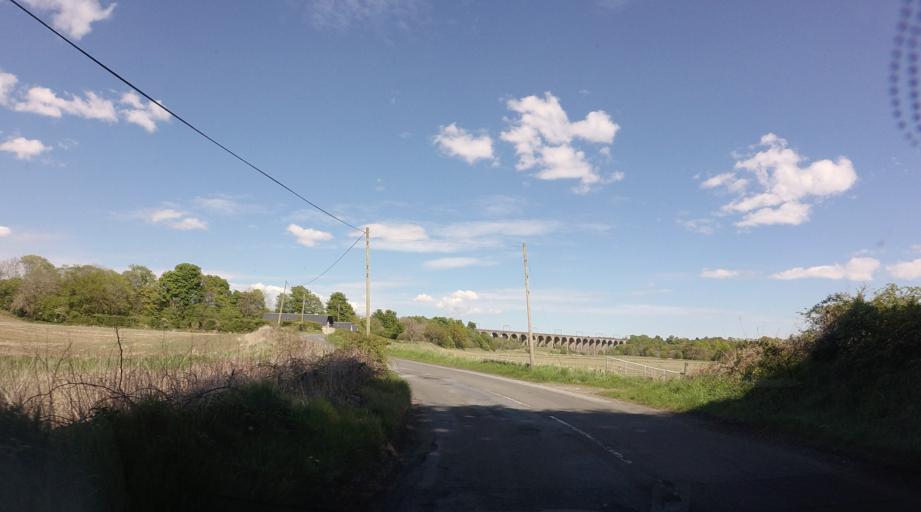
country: GB
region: Scotland
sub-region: West Lothian
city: Linlithgow
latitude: 55.9720
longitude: -3.6436
